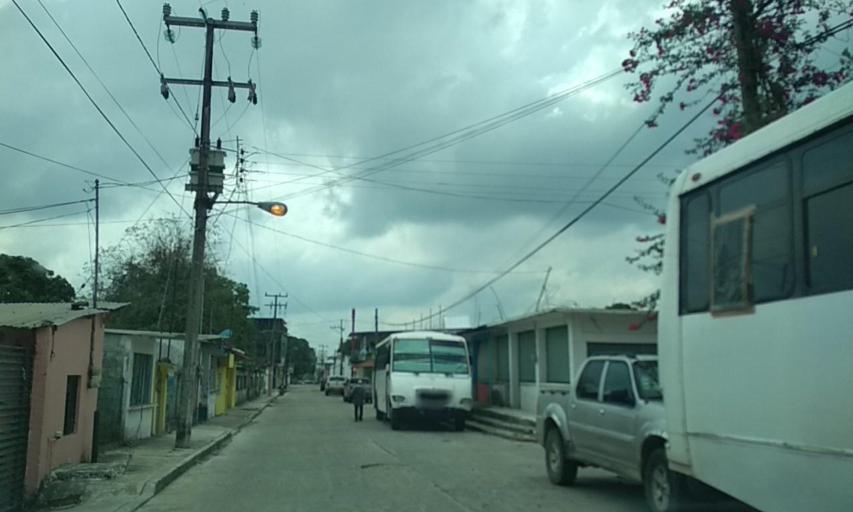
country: MX
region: Veracruz
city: Las Choapas
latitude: 17.8984
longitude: -94.1019
